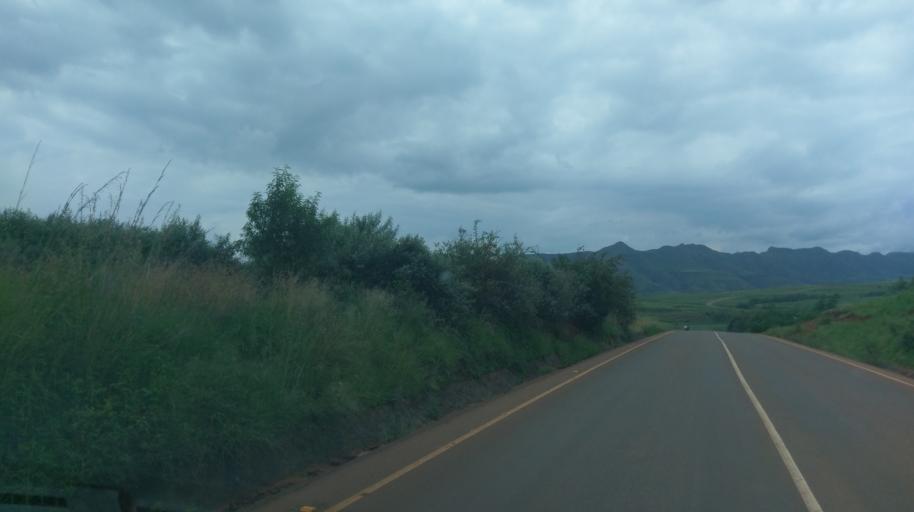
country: LS
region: Leribe
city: Leribe
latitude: -29.0402
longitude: 28.2433
